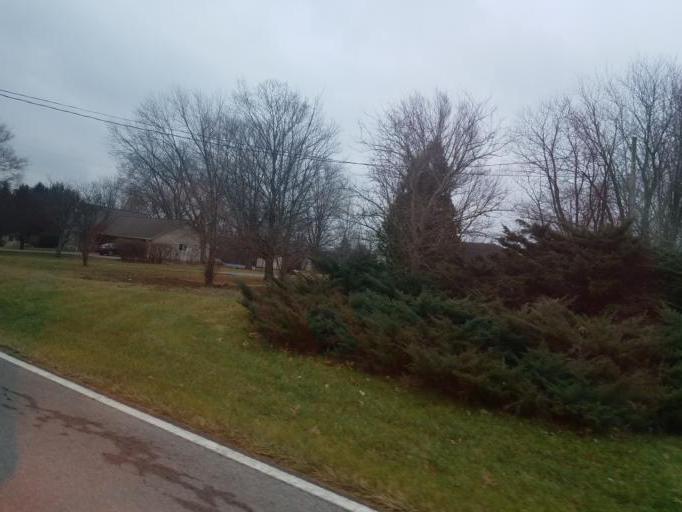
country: US
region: Ohio
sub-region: Franklin County
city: Westerville
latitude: 40.1899
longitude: -82.9228
